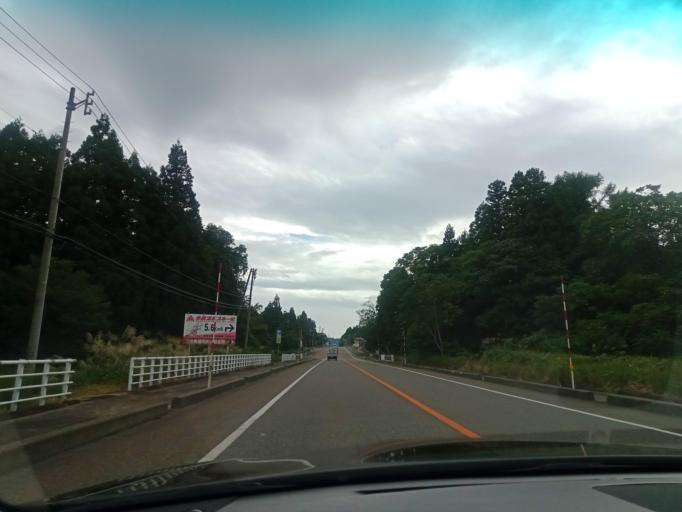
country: JP
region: Niigata
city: Arai
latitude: 36.9513
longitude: 138.2190
